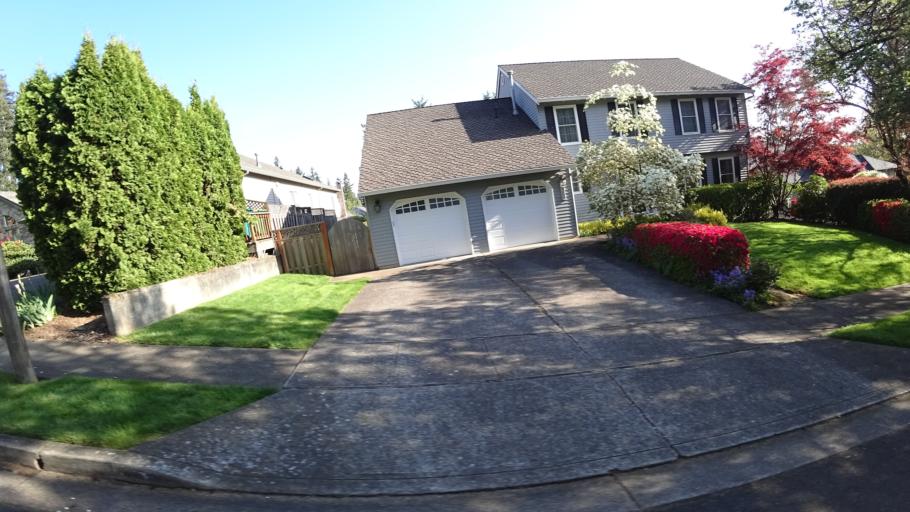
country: US
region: Oregon
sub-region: Washington County
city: Beaverton
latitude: 45.4459
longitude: -122.8359
